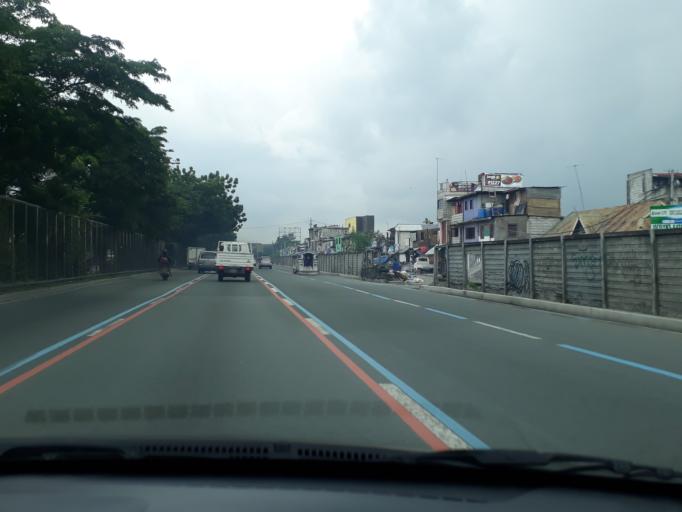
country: PH
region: Calabarzon
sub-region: Province of Rizal
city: Pateros
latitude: 14.5262
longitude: 121.0558
